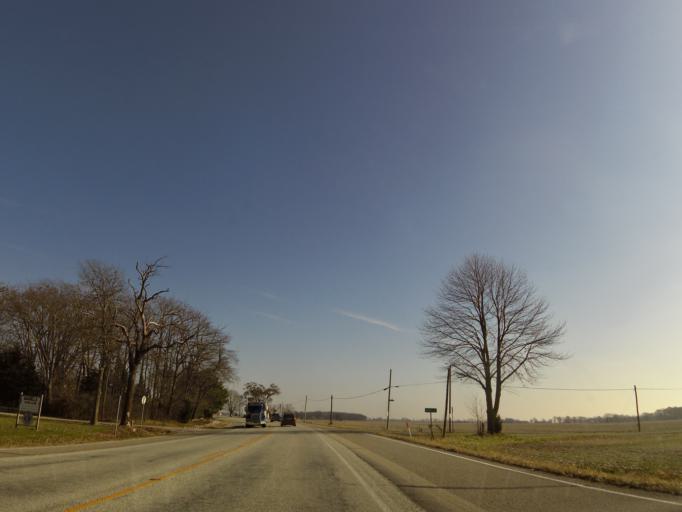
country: US
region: Indiana
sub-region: Shelby County
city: Morristown
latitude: 39.5692
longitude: -85.6227
